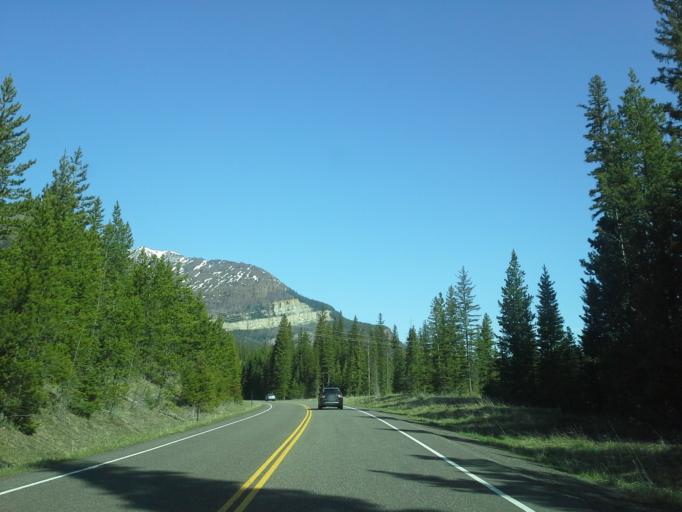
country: US
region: Montana
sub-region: Carbon County
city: Red Lodge
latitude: 44.9743
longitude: -109.8338
